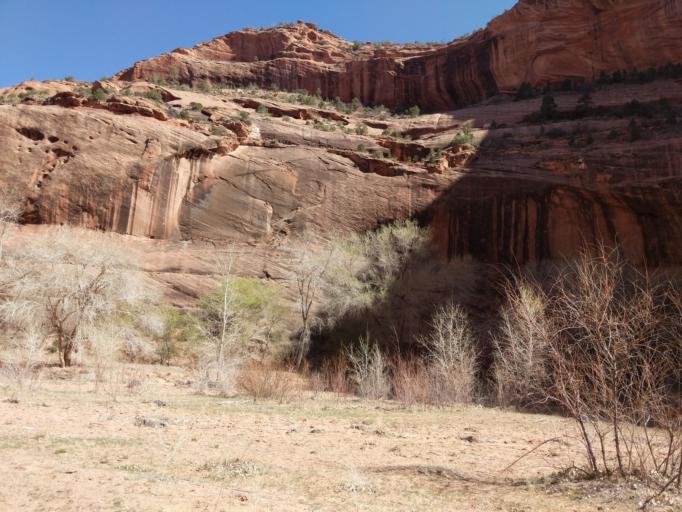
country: US
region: Arizona
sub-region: Apache County
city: Chinle
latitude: 36.1582
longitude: -109.4628
